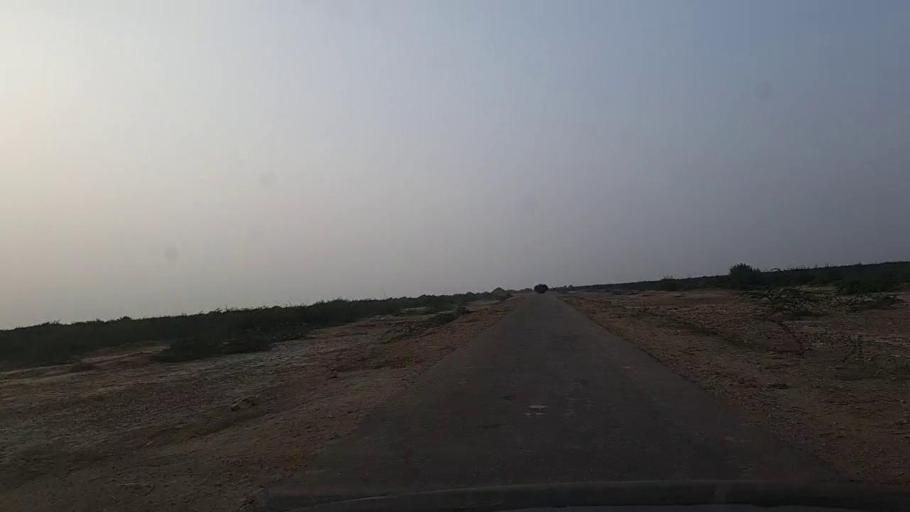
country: PK
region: Sindh
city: Gharo
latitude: 24.7815
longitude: 67.7303
